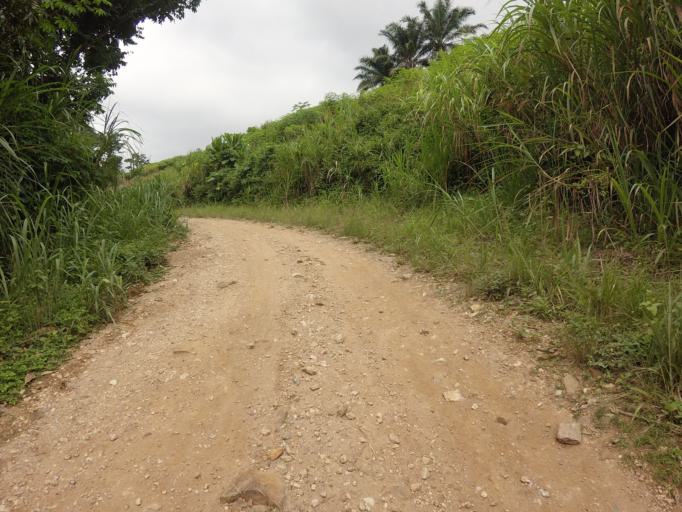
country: GH
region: Volta
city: Kpandu
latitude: 6.8736
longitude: 0.4412
